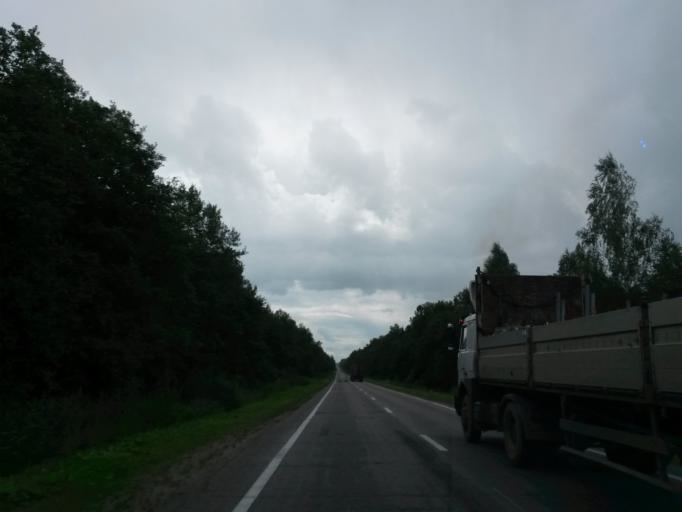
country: RU
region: Jaroslavl
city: Gavrilov-Yam
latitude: 57.4372
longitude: 39.9175
